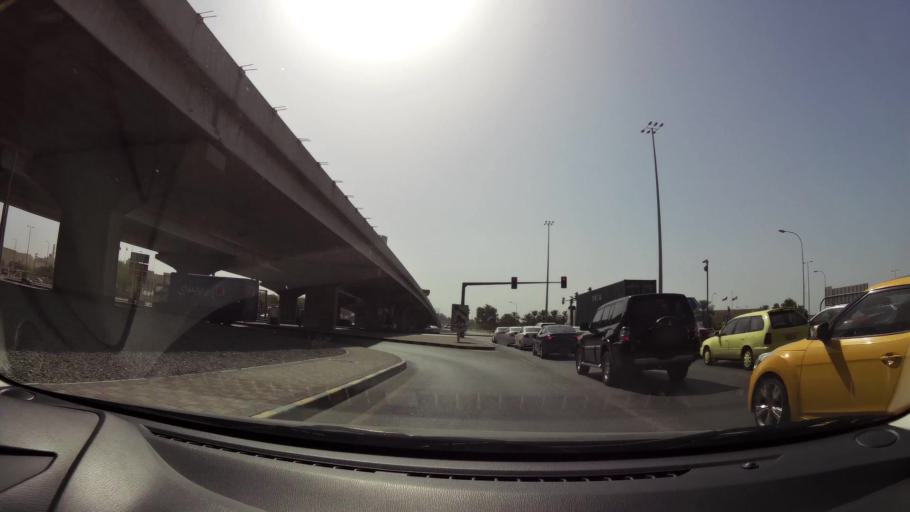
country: OM
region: Muhafazat Masqat
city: Muscat
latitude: 23.6116
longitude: 58.4933
